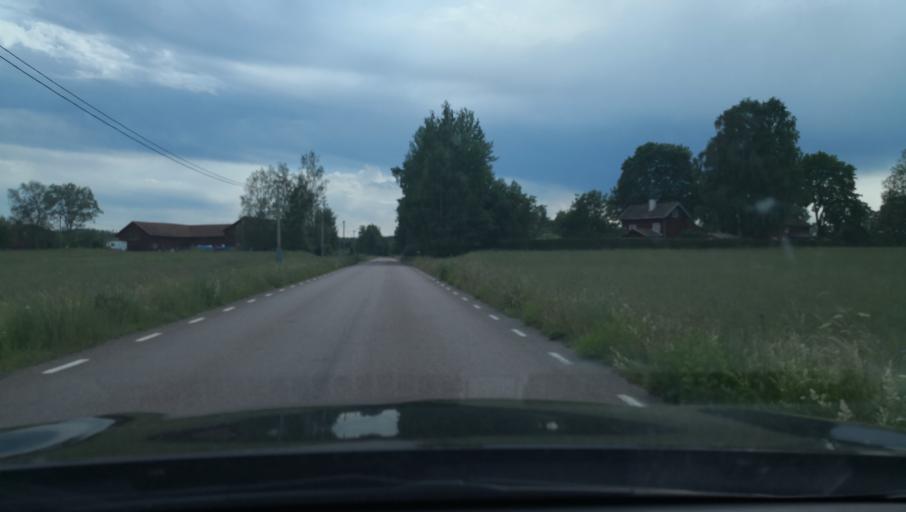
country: SE
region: Dalarna
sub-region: Smedjebackens Kommun
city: Smedjebacken
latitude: 60.0508
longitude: 15.5546
